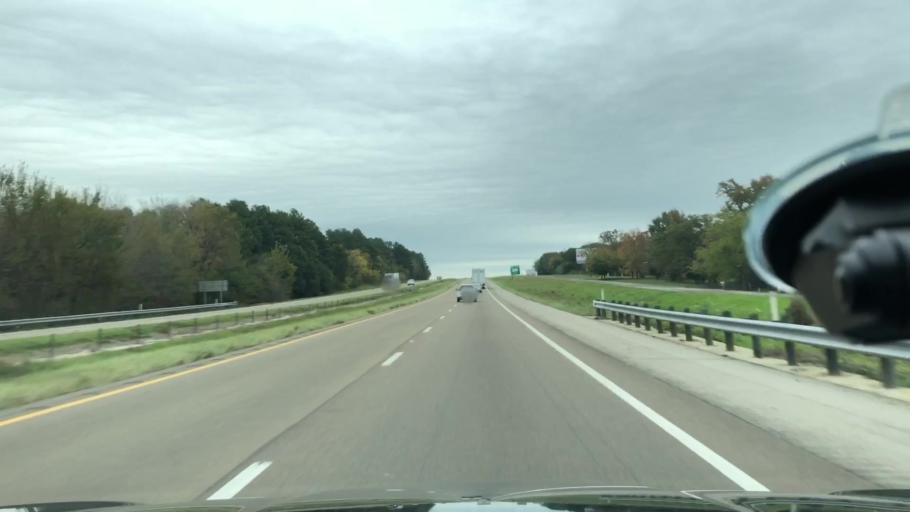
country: US
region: Texas
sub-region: Titus County
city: Mount Pleasant
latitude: 33.1894
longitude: -94.9411
